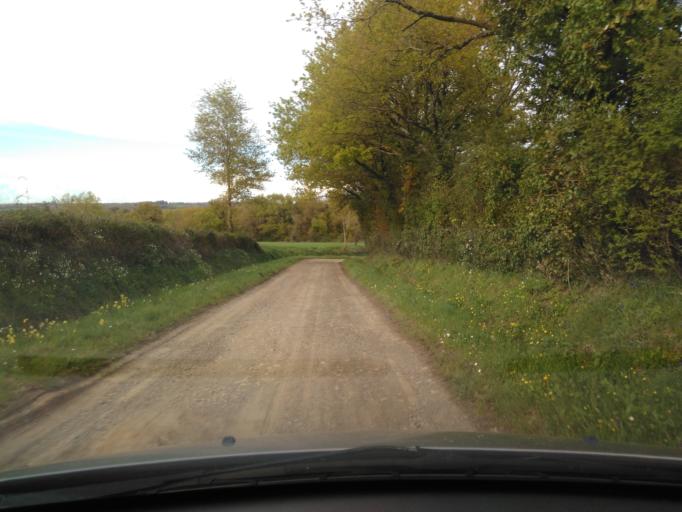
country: FR
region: Pays de la Loire
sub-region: Departement de la Vendee
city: Sainte-Hermine
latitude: 46.6152
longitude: -1.0904
